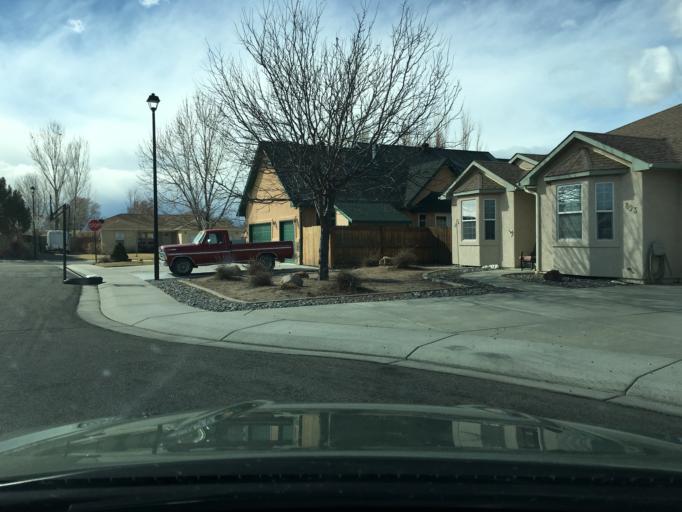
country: US
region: Colorado
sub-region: Mesa County
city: Grand Junction
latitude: 39.1345
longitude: -108.5600
